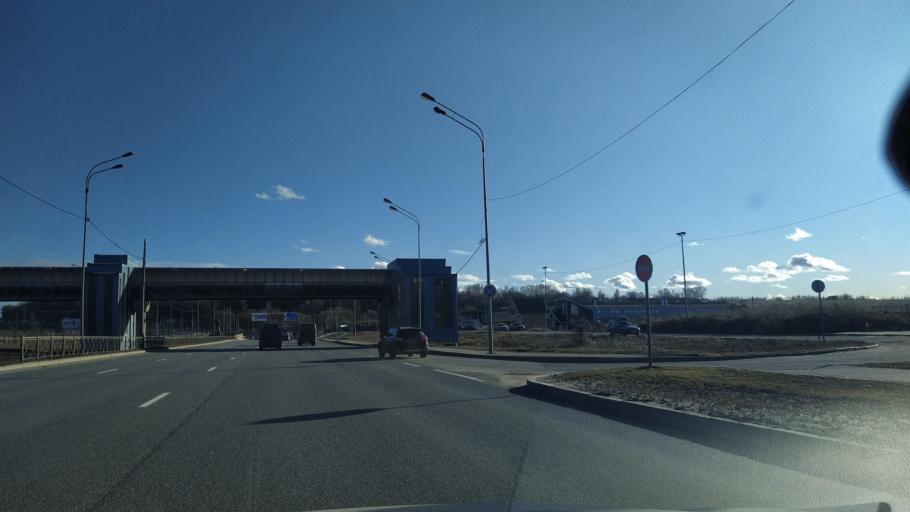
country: RU
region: St.-Petersburg
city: Aleksandrovskaya
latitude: 59.7815
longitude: 30.3249
